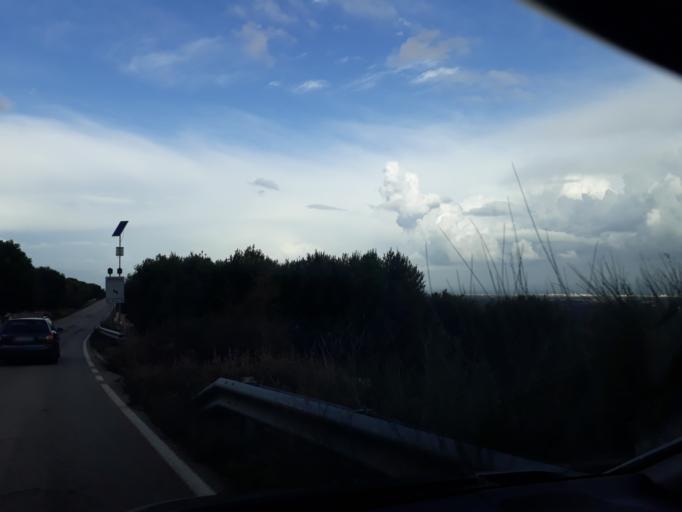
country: IT
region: Apulia
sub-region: Provincia di Brindisi
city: Cisternino
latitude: 40.7771
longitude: 17.4327
